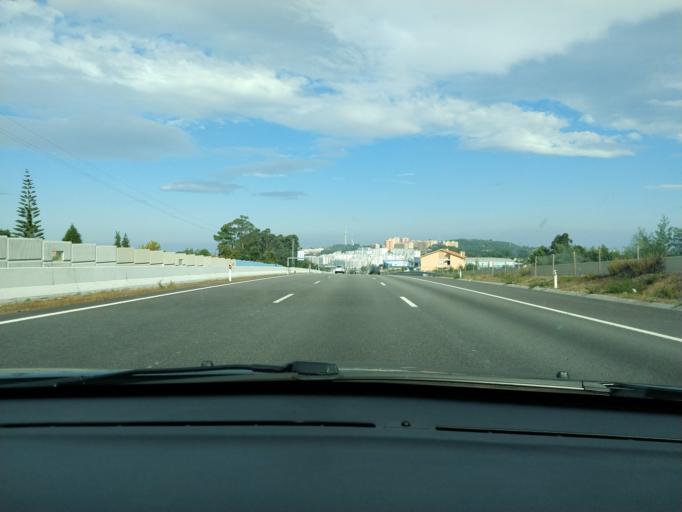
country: PT
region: Porto
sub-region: Vila Nova de Gaia
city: Canelas
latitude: 41.0837
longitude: -8.5836
